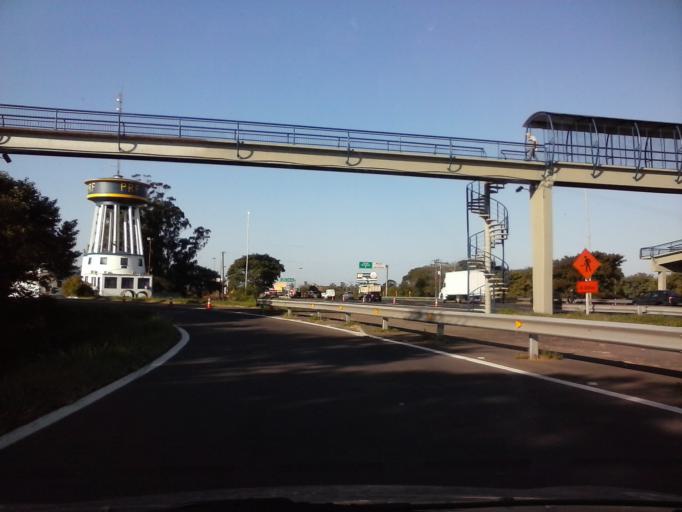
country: BR
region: Rio Grande do Sul
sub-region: Canoas
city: Canoas
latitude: -29.9706
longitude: -51.1723
